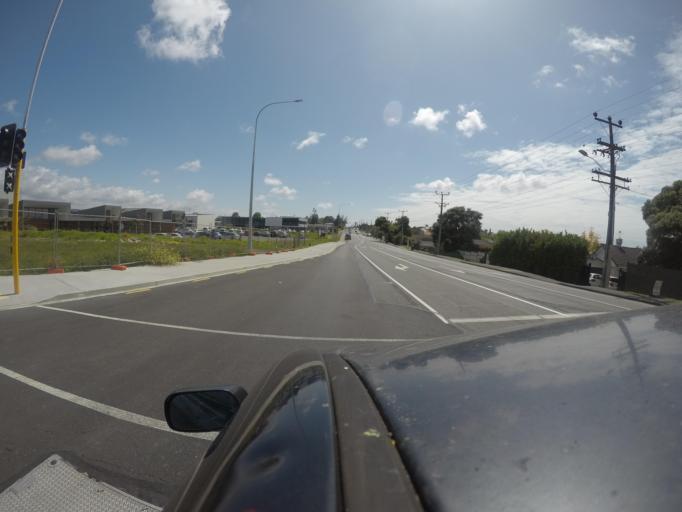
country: NZ
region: Auckland
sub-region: Auckland
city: Rosebank
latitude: -36.8078
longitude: 174.6353
